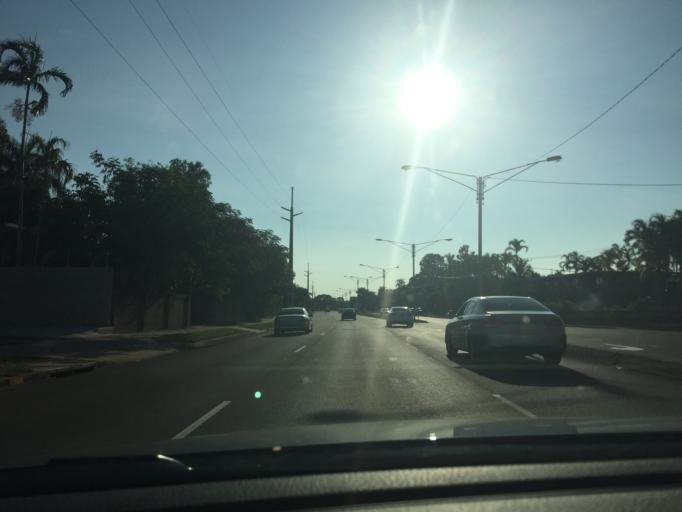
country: AU
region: Northern Territory
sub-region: Darwin
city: Nightcliff
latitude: -12.3828
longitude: 130.8760
